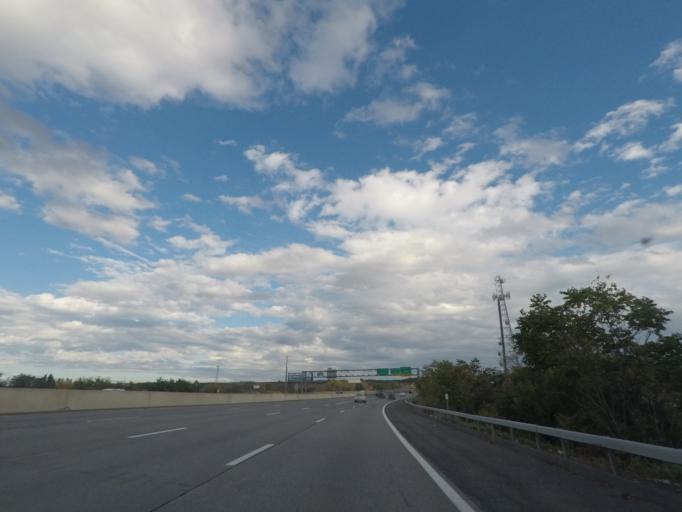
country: US
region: New York
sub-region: Albany County
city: Albany
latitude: 42.6698
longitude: -73.7390
